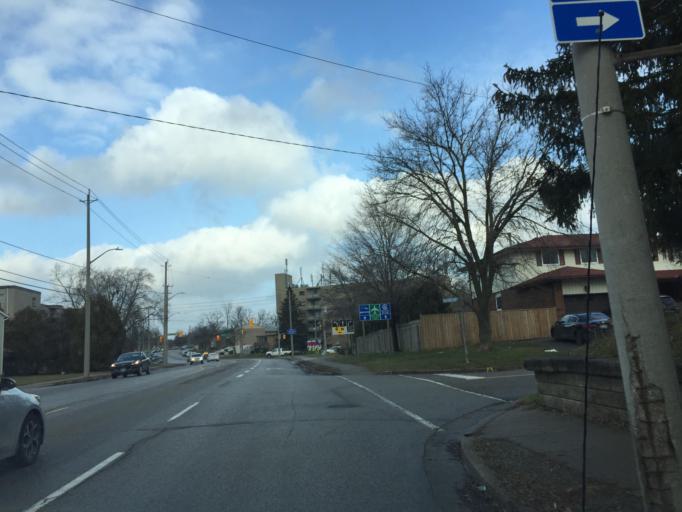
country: CA
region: Ontario
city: Kitchener
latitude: 43.4334
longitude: -80.4289
